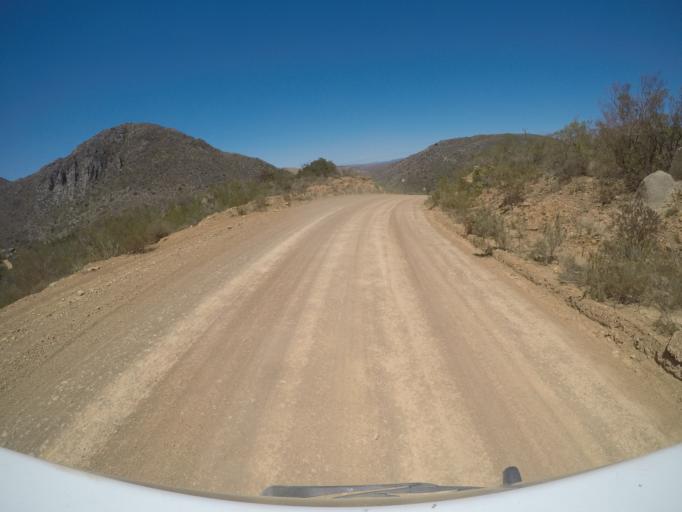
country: ZA
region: Western Cape
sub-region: Overberg District Municipality
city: Grabouw
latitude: -34.1147
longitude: 19.2337
